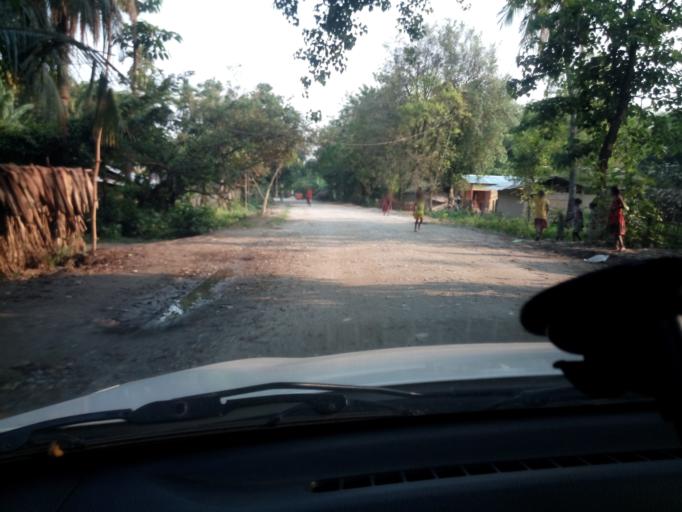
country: IN
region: Assam
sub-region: Udalguri
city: Udalguri
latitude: 26.7270
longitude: 92.0850
